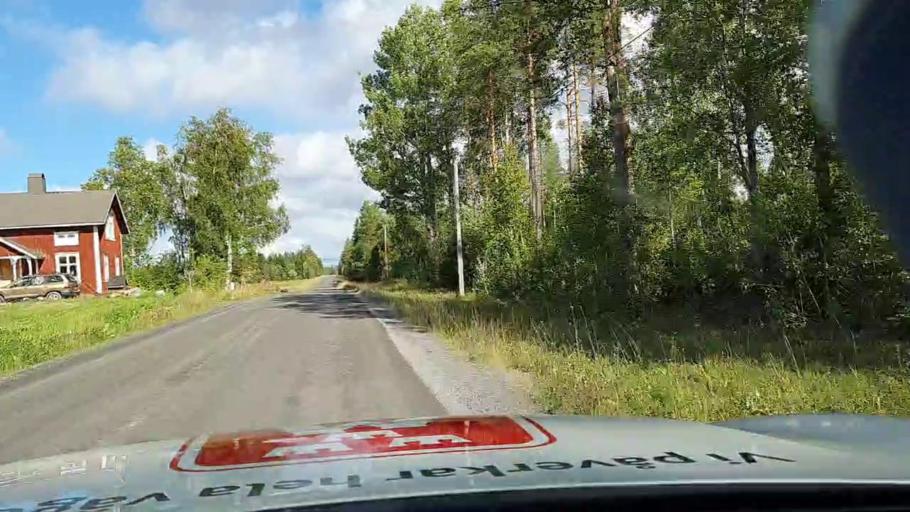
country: SE
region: Jaemtland
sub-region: Stroemsunds Kommun
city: Stroemsund
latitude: 63.6857
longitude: 15.1212
